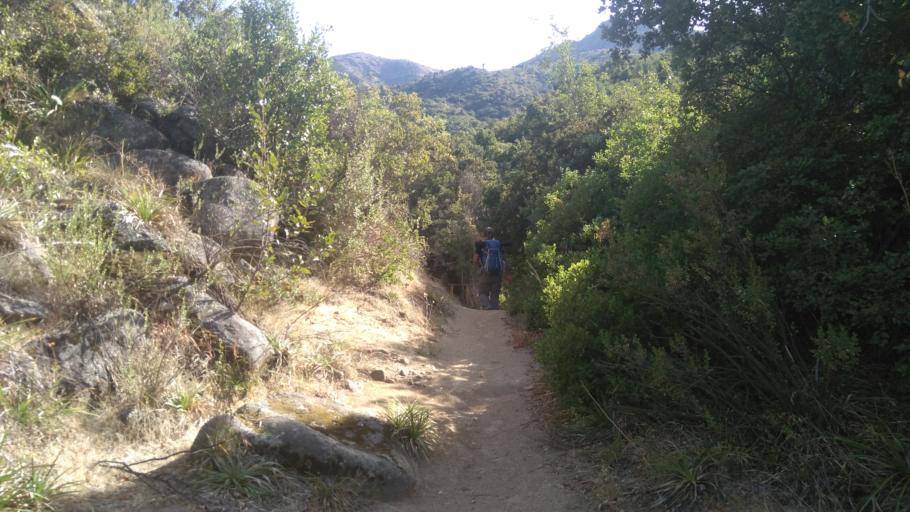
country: CL
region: Santiago Metropolitan
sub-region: Provincia de Cordillera
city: Puente Alto
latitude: -33.7241
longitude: -70.4683
